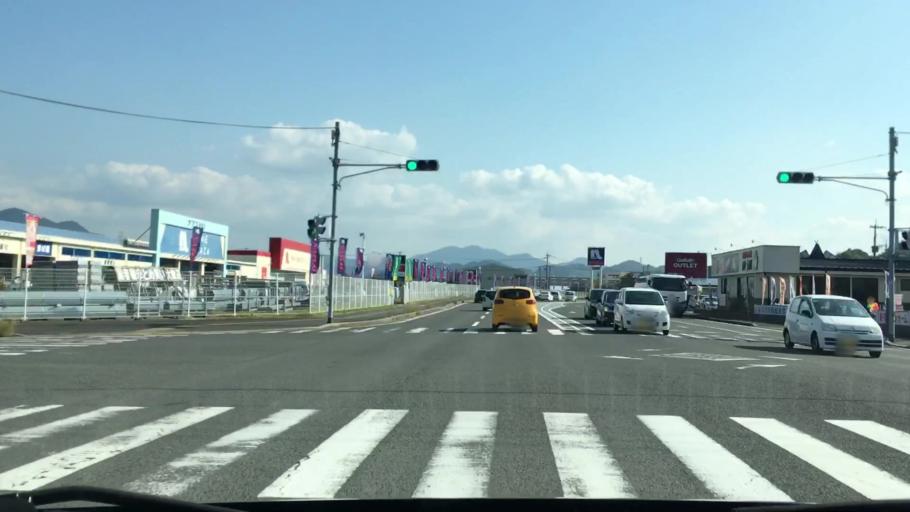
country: JP
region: Nagasaki
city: Togitsu
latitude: 32.8500
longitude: 129.8285
